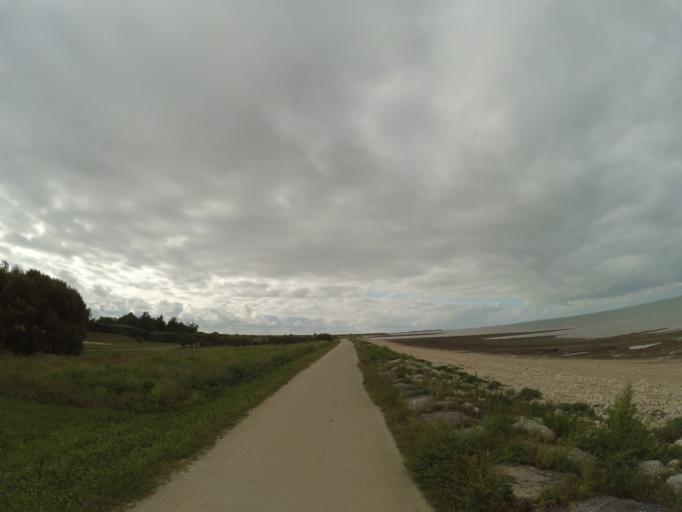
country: FR
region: Poitou-Charentes
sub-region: Departement de la Charente-Maritime
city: La Rochelle
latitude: 46.1364
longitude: -1.1526
